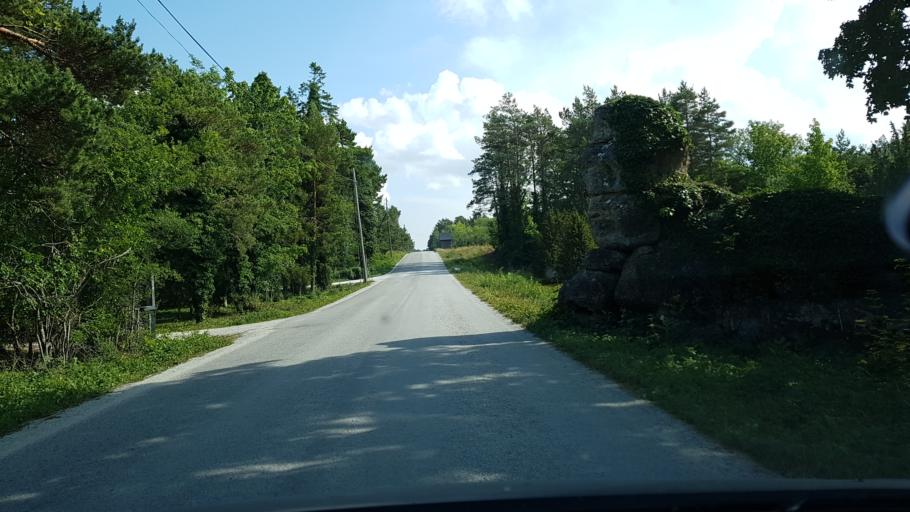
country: SE
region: Gotland
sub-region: Gotland
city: Visby
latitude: 57.8227
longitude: 18.5158
